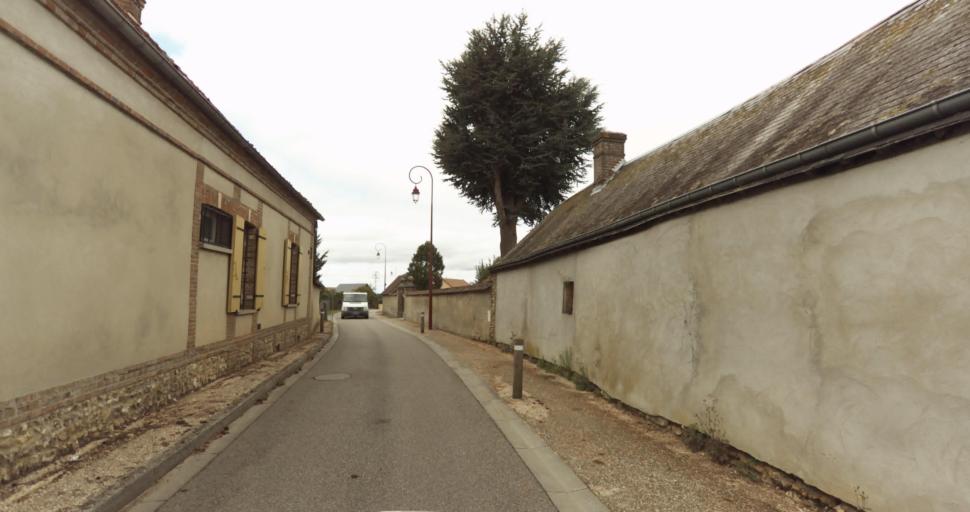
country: FR
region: Haute-Normandie
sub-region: Departement de l'Eure
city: Evreux
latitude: 48.9379
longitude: 1.1949
